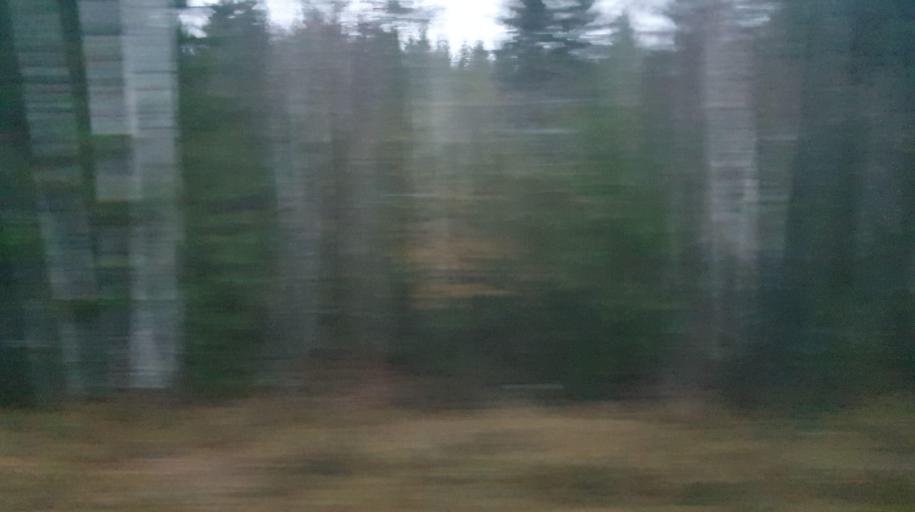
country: NO
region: Buskerud
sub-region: Krodsherad
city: Noresund
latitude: 60.1461
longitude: 9.7652
